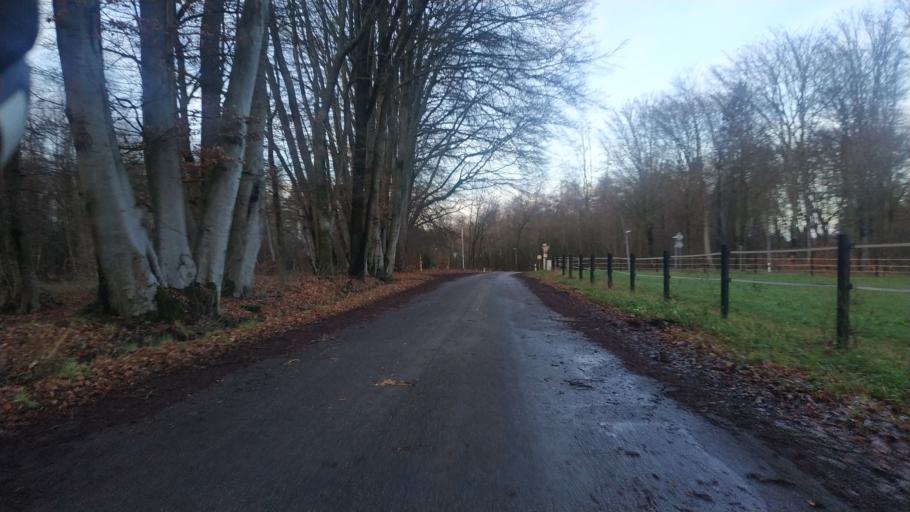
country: DE
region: North Rhine-Westphalia
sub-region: Regierungsbezirk Munster
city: Mettingen
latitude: 52.3008
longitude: 7.7671
